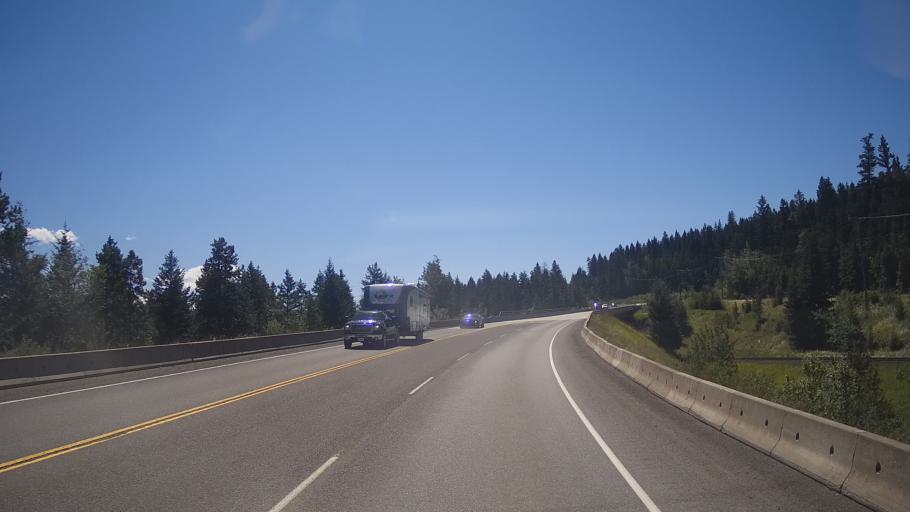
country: CA
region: British Columbia
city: Cache Creek
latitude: 51.6197
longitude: -121.2912
